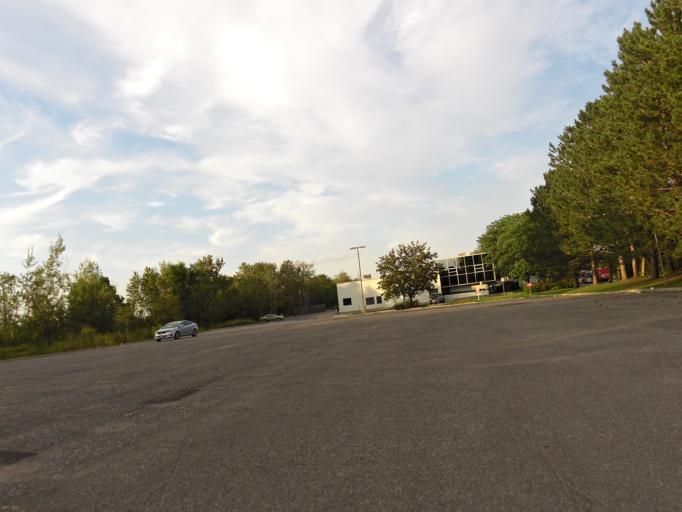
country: CA
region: Ontario
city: Bells Corners
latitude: 45.3239
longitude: -75.8380
